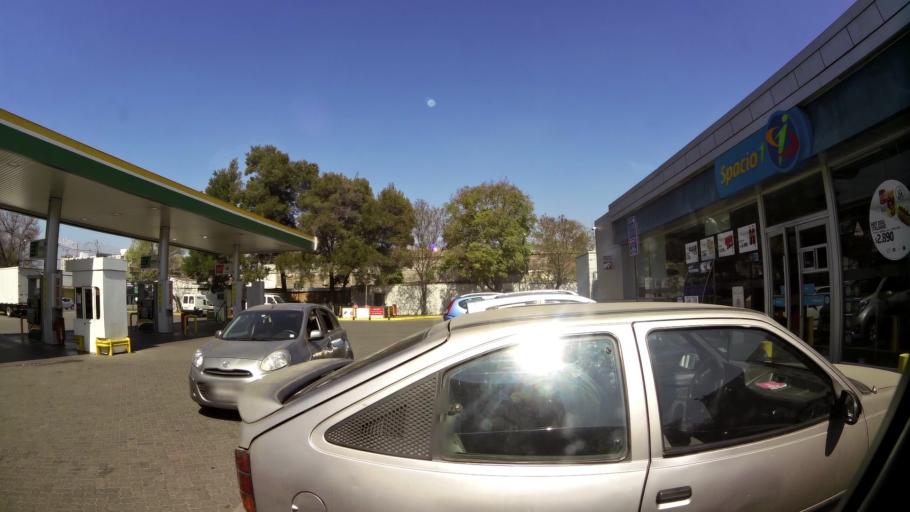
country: CL
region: Santiago Metropolitan
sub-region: Provincia de Santiago
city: Santiago
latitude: -33.4220
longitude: -70.6632
